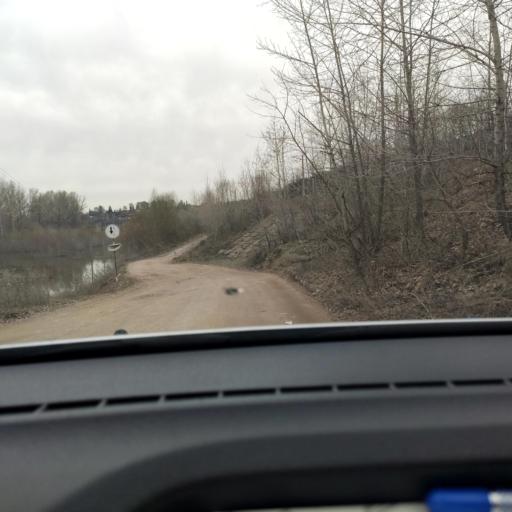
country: RU
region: Bashkortostan
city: Avdon
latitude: 54.6140
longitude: 55.6069
